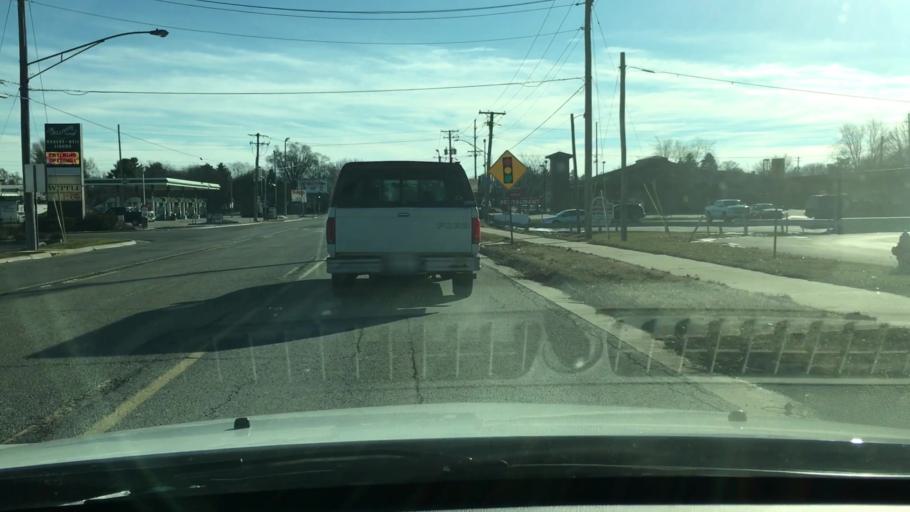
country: US
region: Illinois
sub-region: LaSalle County
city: Mendota
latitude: 41.5569
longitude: -89.1278
